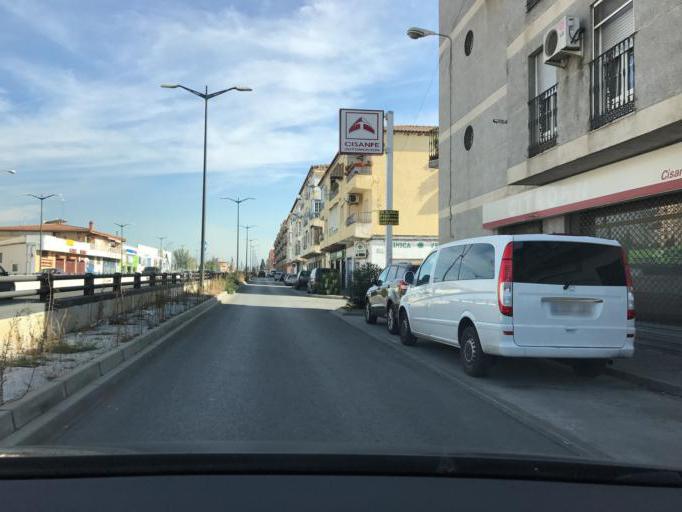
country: ES
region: Andalusia
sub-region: Provincia de Granada
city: Atarfe
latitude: 37.1924
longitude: -3.7171
